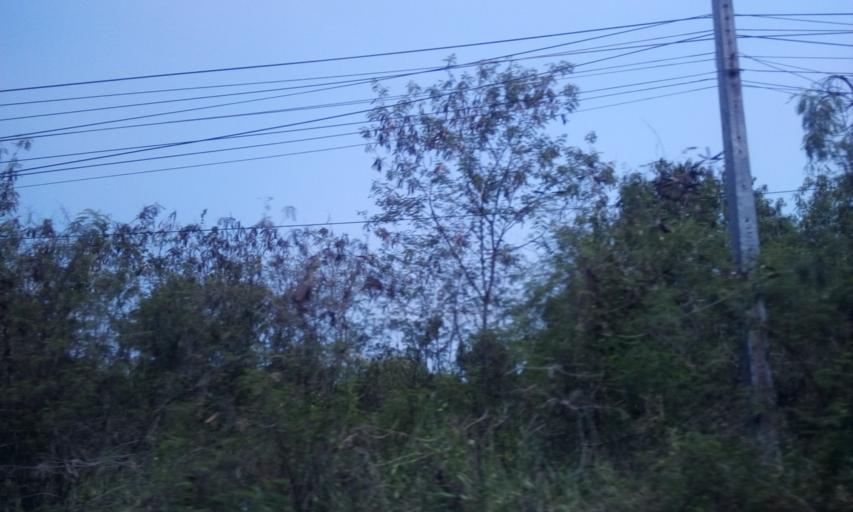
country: TH
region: Chachoengsao
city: Chachoengsao
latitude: 13.7685
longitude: 101.0683
